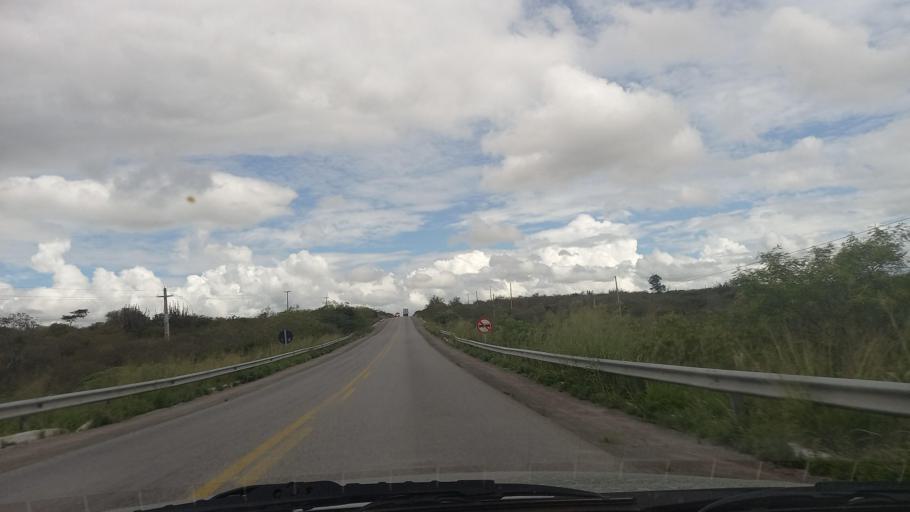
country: BR
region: Pernambuco
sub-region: Cachoeirinha
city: Cachoeirinha
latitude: -8.3559
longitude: -36.1720
